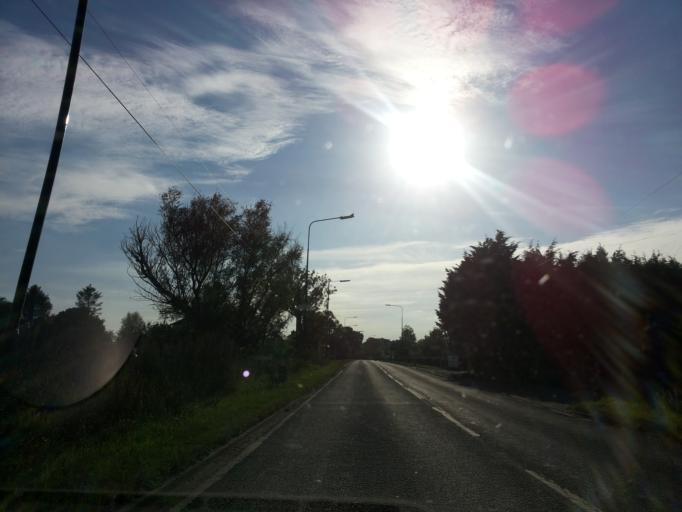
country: GB
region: England
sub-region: Doncaster
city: Hatfield
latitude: 53.5822
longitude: -0.9650
